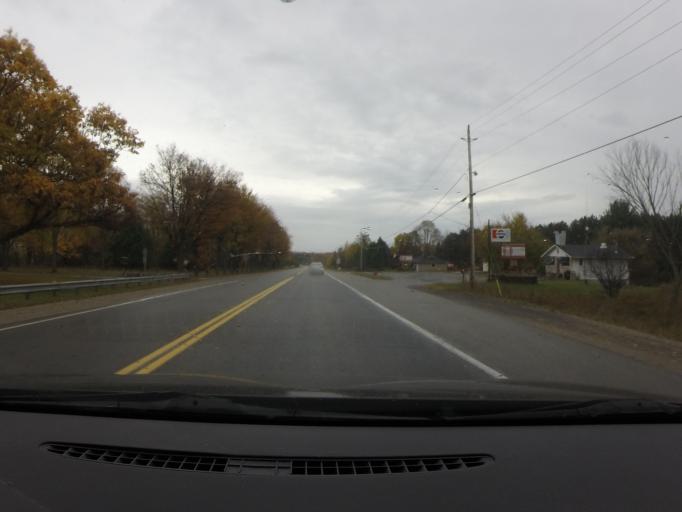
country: CA
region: Ontario
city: Carleton Place
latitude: 45.0590
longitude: -76.2495
